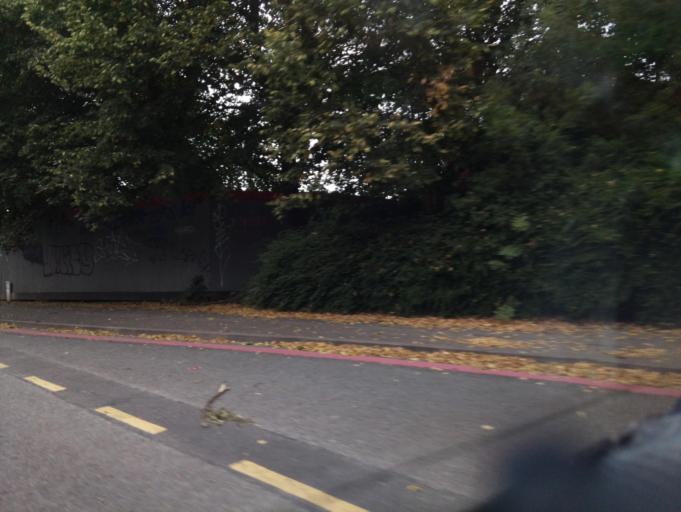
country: GB
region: England
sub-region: Stoke-on-Trent
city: Stoke-on-Trent
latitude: 53.0048
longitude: -2.1775
